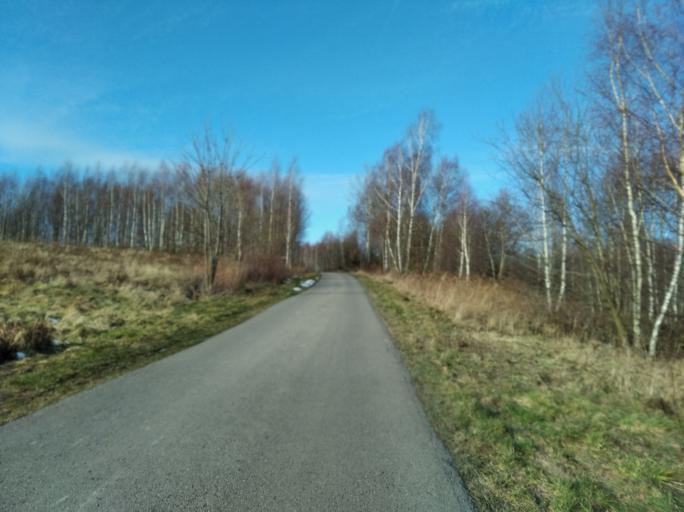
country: PL
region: Subcarpathian Voivodeship
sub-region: Powiat strzyzowski
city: Gwoznica Gorna
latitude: 49.8213
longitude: 21.9883
